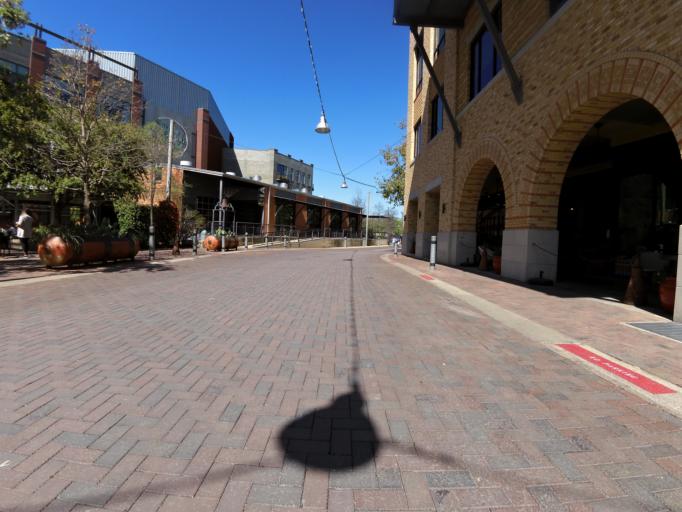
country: US
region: Texas
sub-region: Bexar County
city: San Antonio
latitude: 29.4425
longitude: -98.4801
